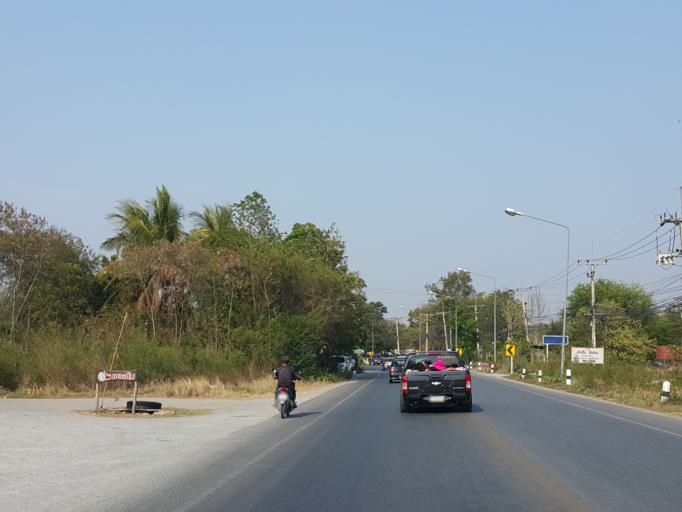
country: TH
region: Suphan Buri
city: Sam Chuk
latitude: 14.7565
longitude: 100.0849
